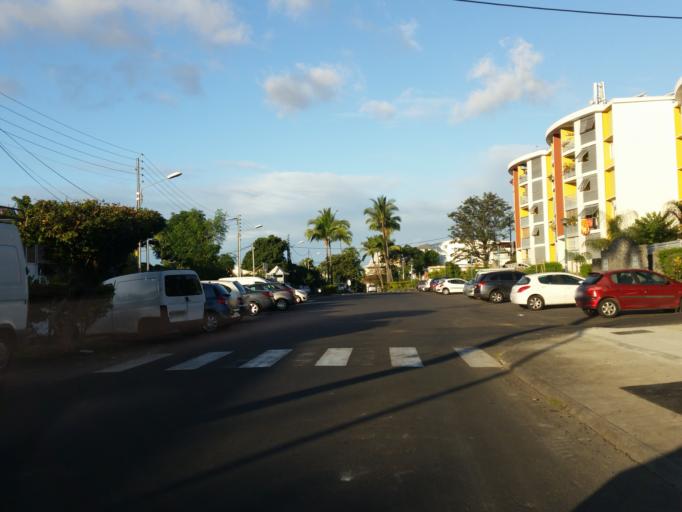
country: RE
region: Reunion
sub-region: Reunion
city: Saint-Denis
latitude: -20.8915
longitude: 55.4506
